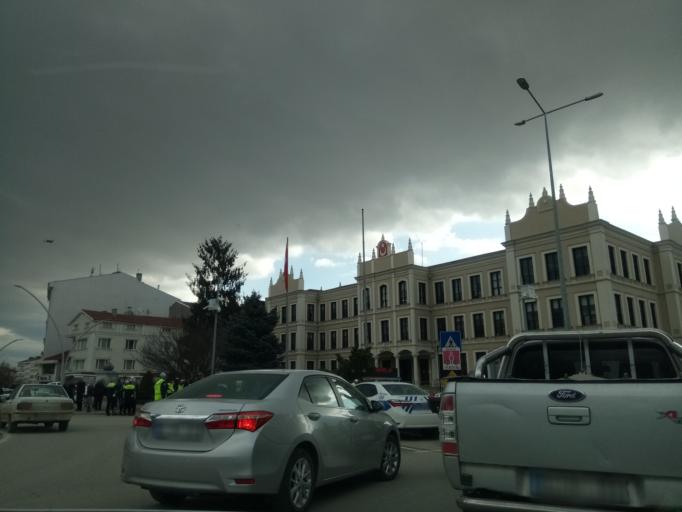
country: TR
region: Bolu
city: Bolu
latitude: 40.6935
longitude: 31.5322
